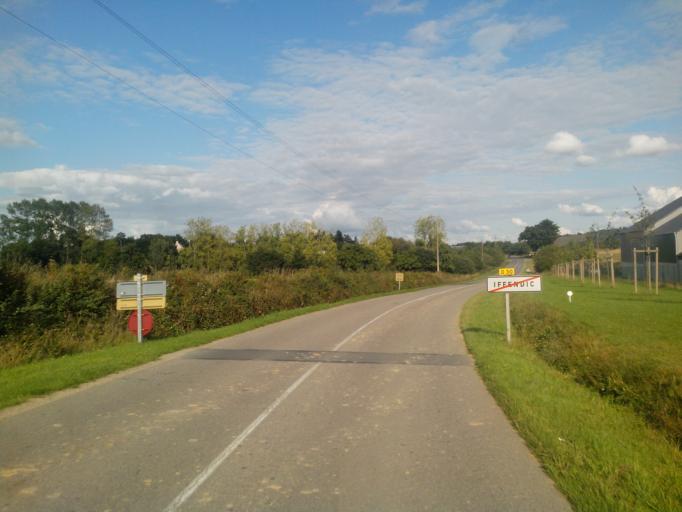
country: FR
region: Brittany
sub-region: Departement d'Ille-et-Vilaine
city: Iffendic
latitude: 48.1322
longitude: -2.0215
